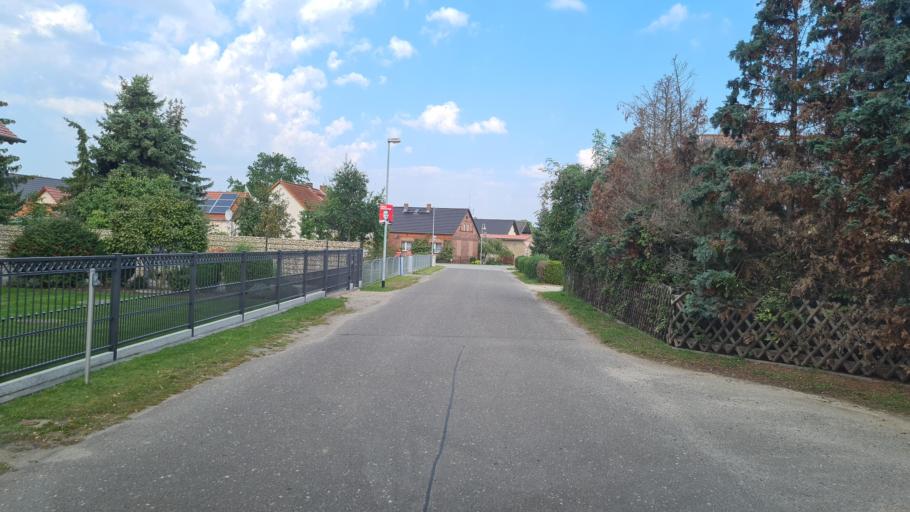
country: DE
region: Brandenburg
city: Drebkau
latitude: 51.6782
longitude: 14.2030
